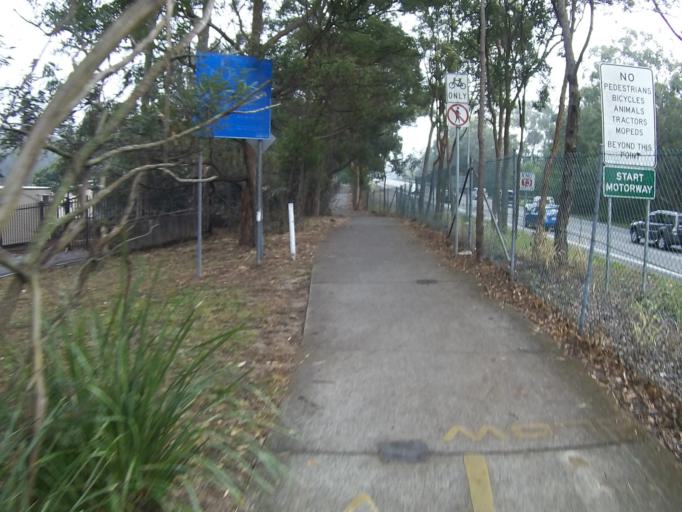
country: AU
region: Queensland
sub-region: Brisbane
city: Nathan
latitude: -27.5501
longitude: 153.0657
